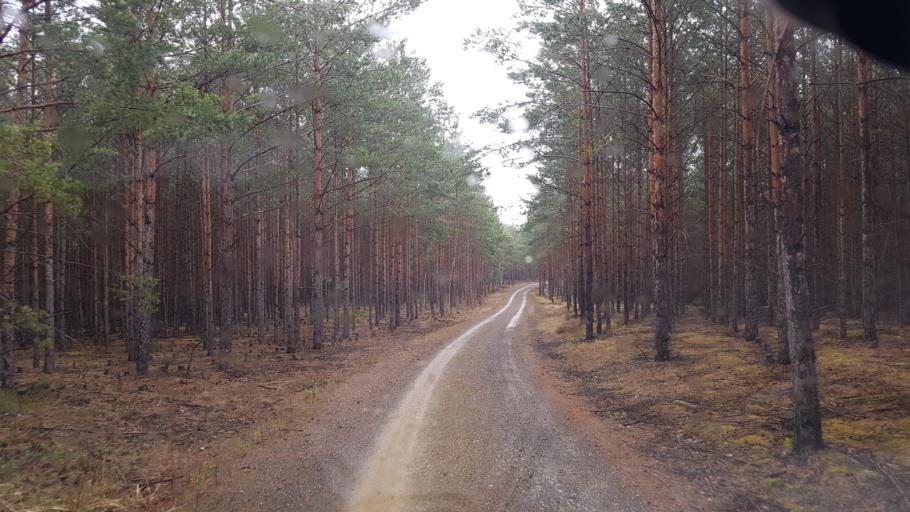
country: DE
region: Brandenburg
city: Grossraschen
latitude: 51.6076
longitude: 13.9764
